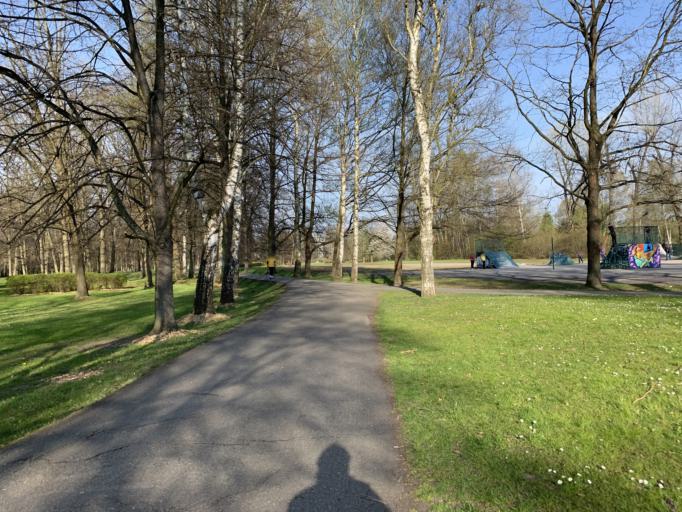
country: CZ
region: Jihocesky
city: Litvinovice
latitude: 48.9688
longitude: 14.4587
